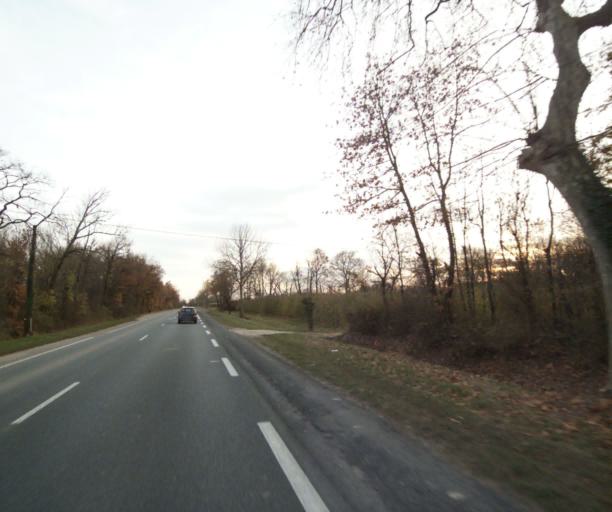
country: FR
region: Poitou-Charentes
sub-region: Departement de la Charente-Maritime
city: Fontcouverte
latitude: 45.7824
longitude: -0.5707
